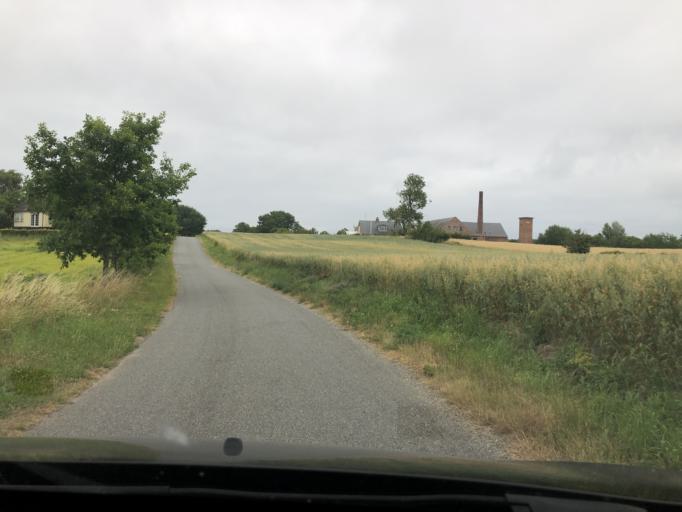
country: DK
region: South Denmark
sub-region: AEro Kommune
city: AEroskobing
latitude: 54.9117
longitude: 10.2941
